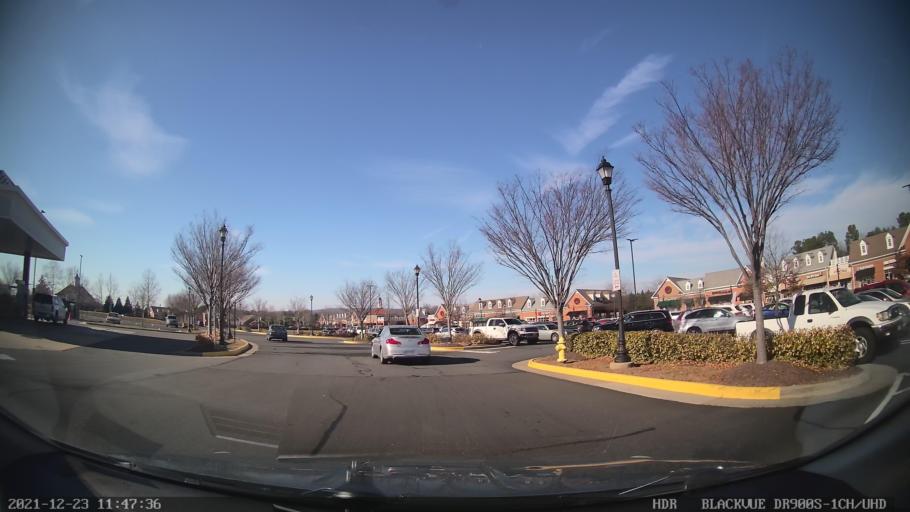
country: US
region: Virginia
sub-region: Prince William County
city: Haymarket
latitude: 38.8441
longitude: -77.6392
